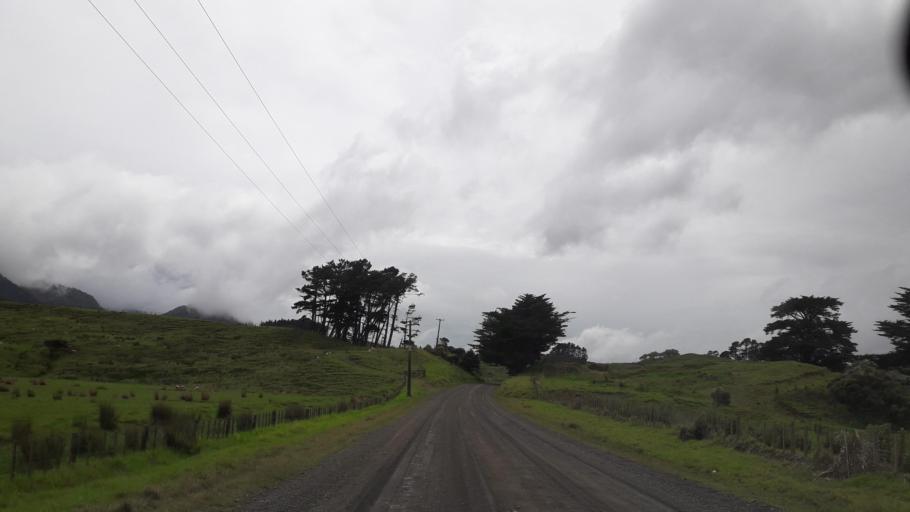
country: NZ
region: Northland
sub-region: Far North District
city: Ahipara
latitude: -35.4207
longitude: 173.3609
